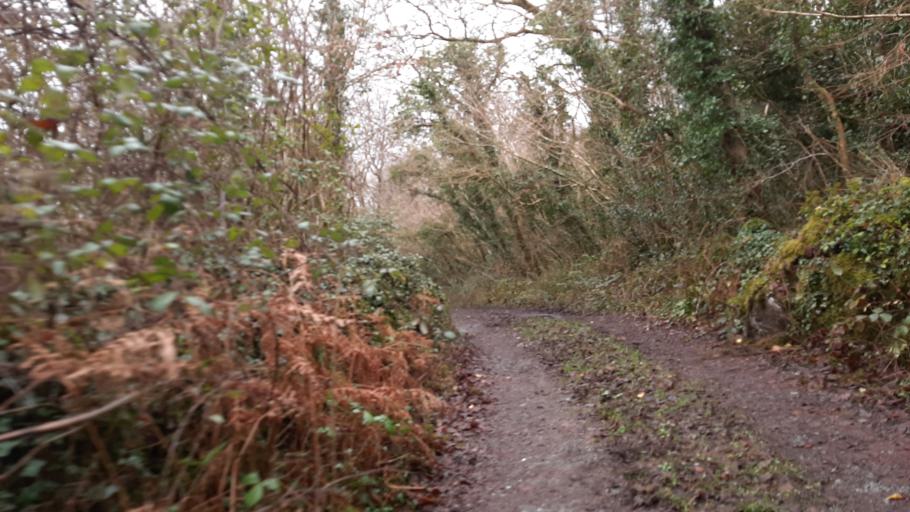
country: IE
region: Connaught
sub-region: County Galway
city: Gaillimh
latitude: 53.2952
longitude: -9.0659
